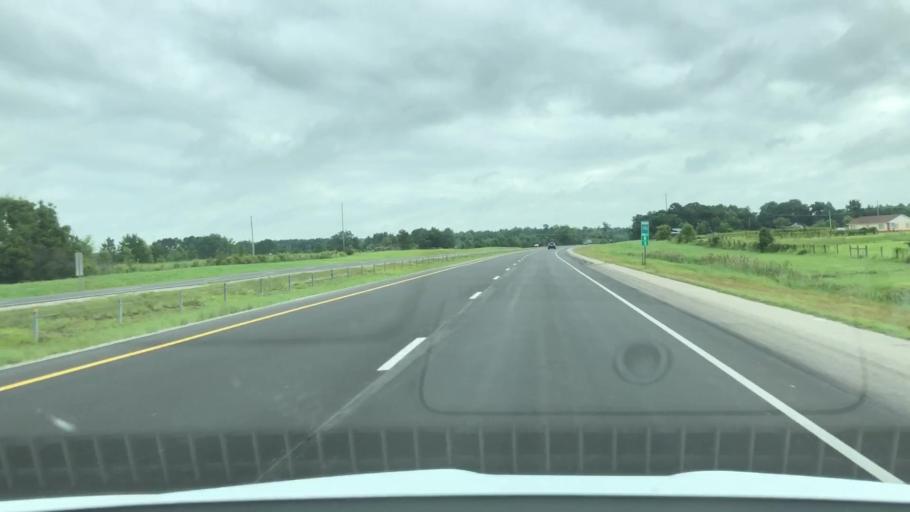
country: US
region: North Carolina
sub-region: Wilson County
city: Lucama
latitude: 35.6302
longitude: -77.9730
